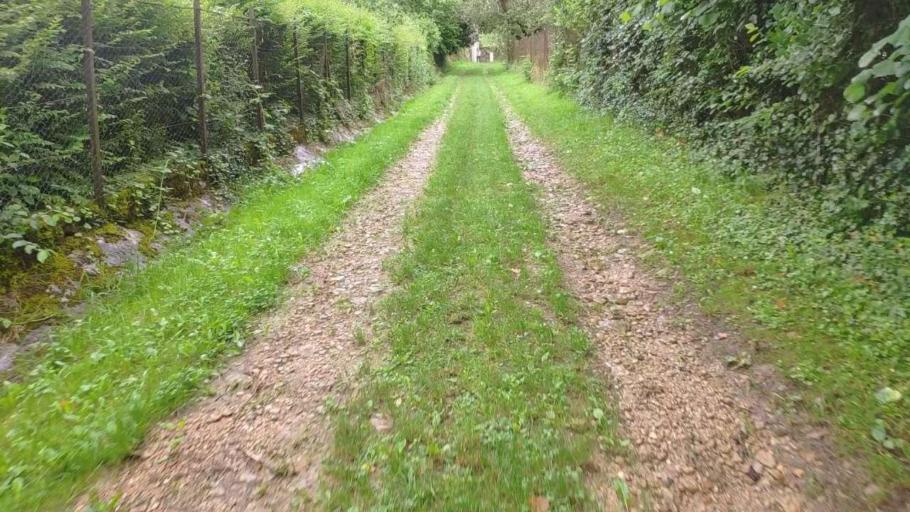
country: FR
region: Franche-Comte
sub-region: Departement du Jura
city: Poligny
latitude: 46.7881
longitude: 5.6181
